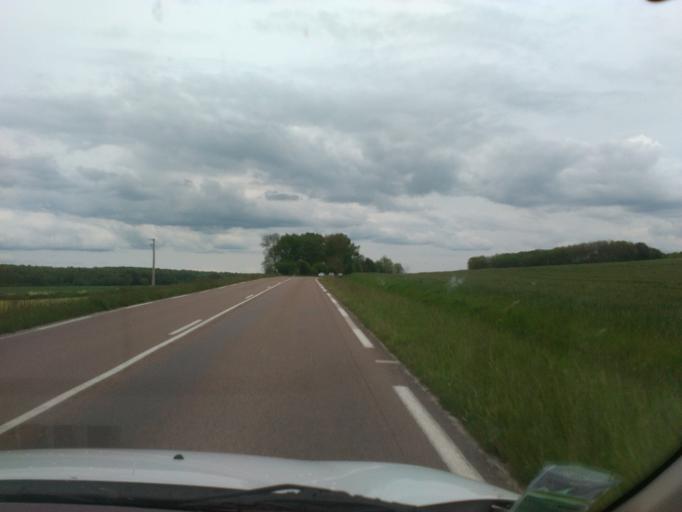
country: FR
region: Champagne-Ardenne
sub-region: Departement de l'Aube
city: Vendeuvre-sur-Barse
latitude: 48.2357
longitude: 4.4204
